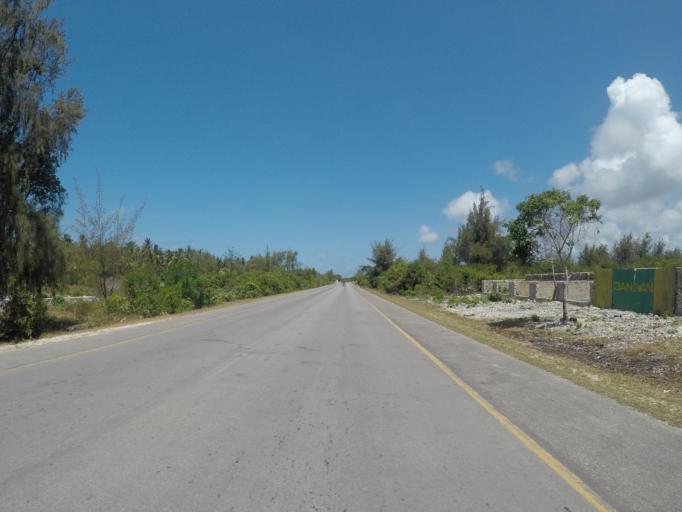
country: TZ
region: Zanzibar Central/South
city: Nganane
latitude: -6.3200
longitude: 39.5436
